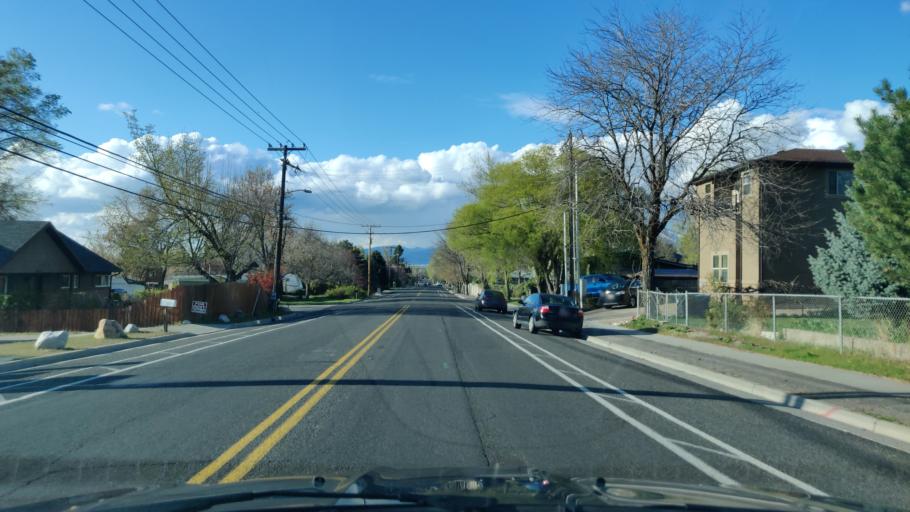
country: US
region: Utah
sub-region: Salt Lake County
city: Cottonwood Heights
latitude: 40.6294
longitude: -111.8247
